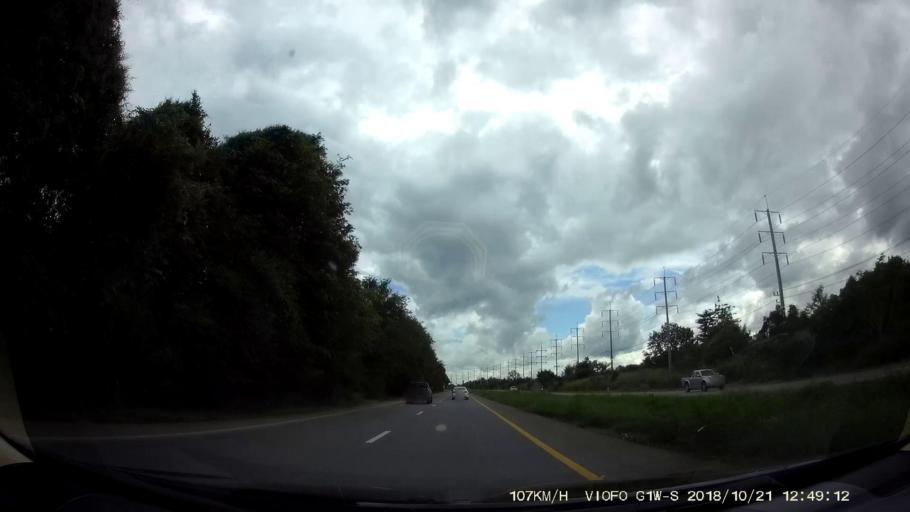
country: TH
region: Nakhon Ratchasima
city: Amphoe Sikhiu
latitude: 14.9000
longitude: 101.6841
